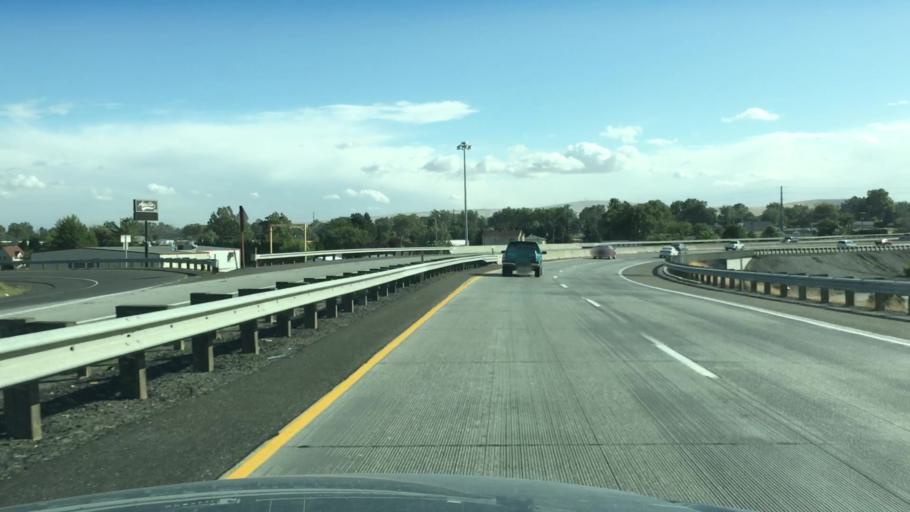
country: US
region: Washington
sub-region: Benton County
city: Kennewick
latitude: 46.2179
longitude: -119.1381
